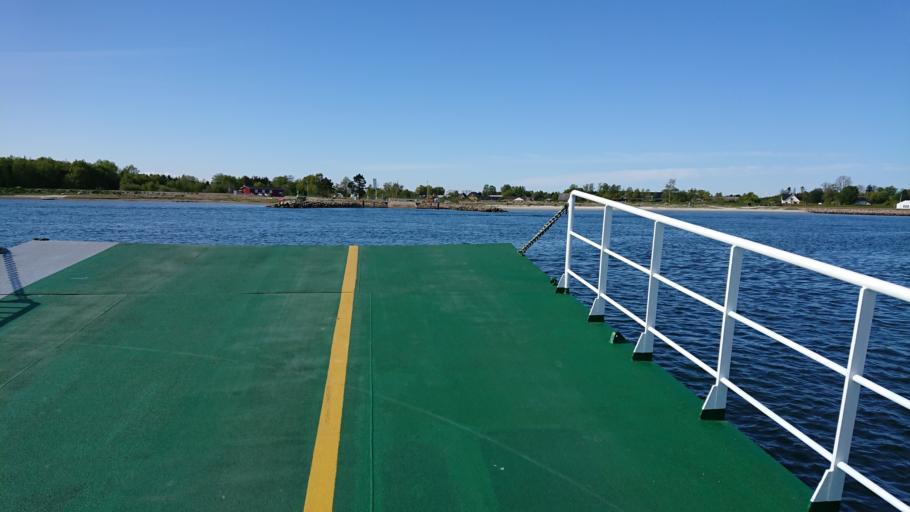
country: DK
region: Central Jutland
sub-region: Norddjurs Kommune
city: Allingabro
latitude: 56.6079
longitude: 10.3015
